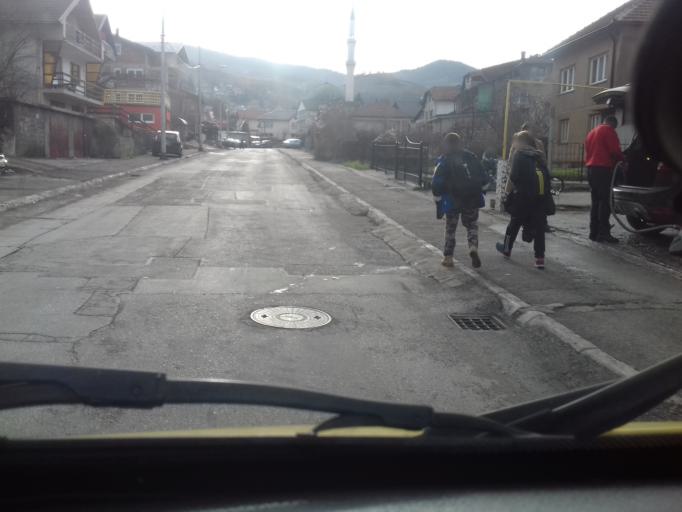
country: BA
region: Federation of Bosnia and Herzegovina
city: Zenica
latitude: 44.1918
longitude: 17.9091
